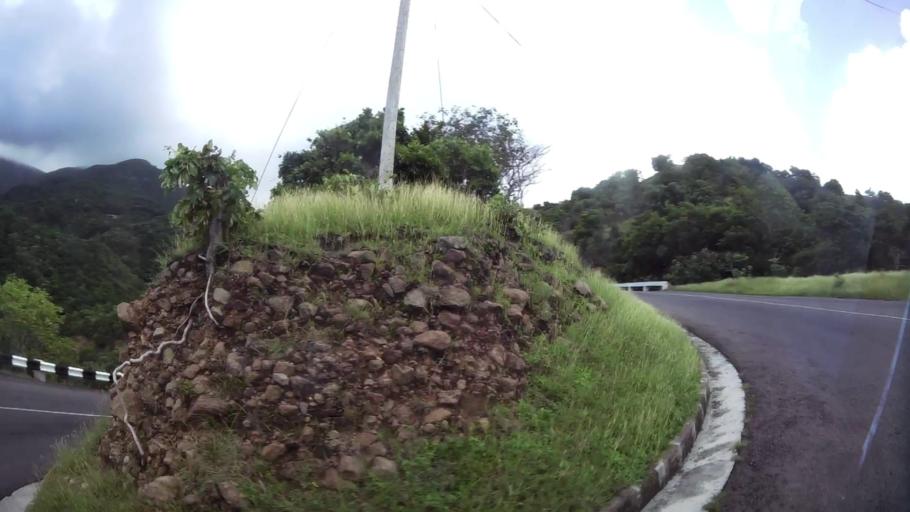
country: MS
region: Saint Peter
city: Saint Peters
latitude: 16.7779
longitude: -62.2090
